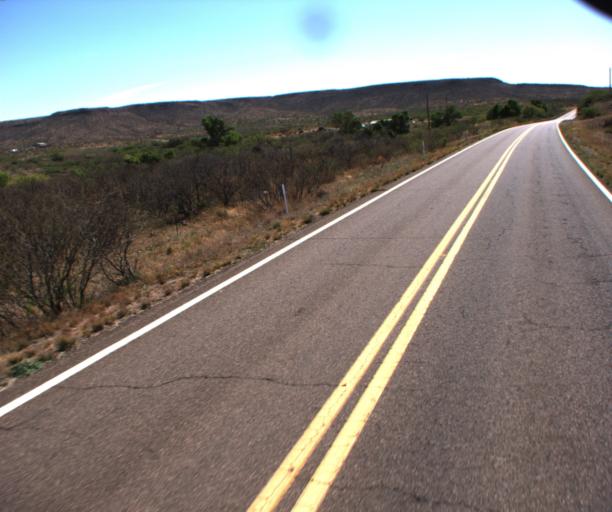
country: US
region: Arizona
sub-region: Cochise County
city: Douglas
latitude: 31.4788
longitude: -109.4017
